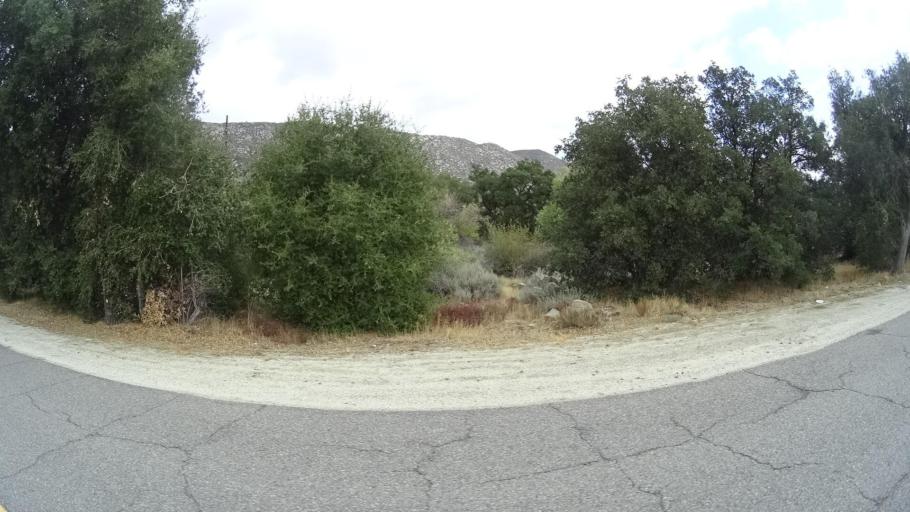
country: US
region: California
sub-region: San Diego County
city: Pine Valley
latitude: 32.7686
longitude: -116.4929
